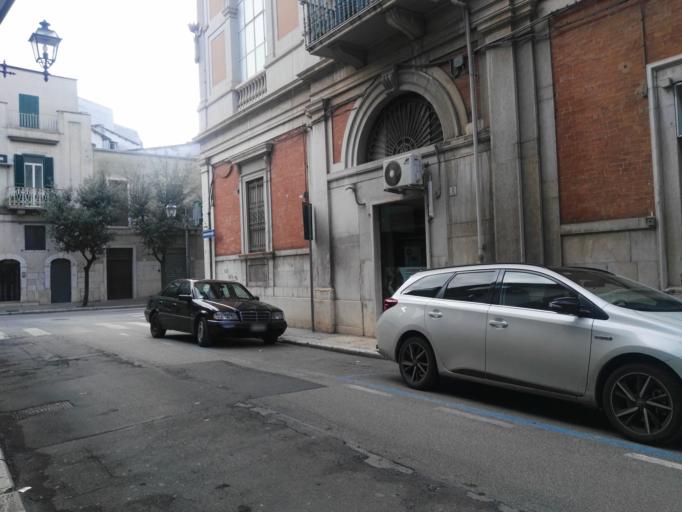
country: IT
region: Apulia
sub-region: Provincia di Barletta - Andria - Trani
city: Andria
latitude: 41.2254
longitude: 16.2999
